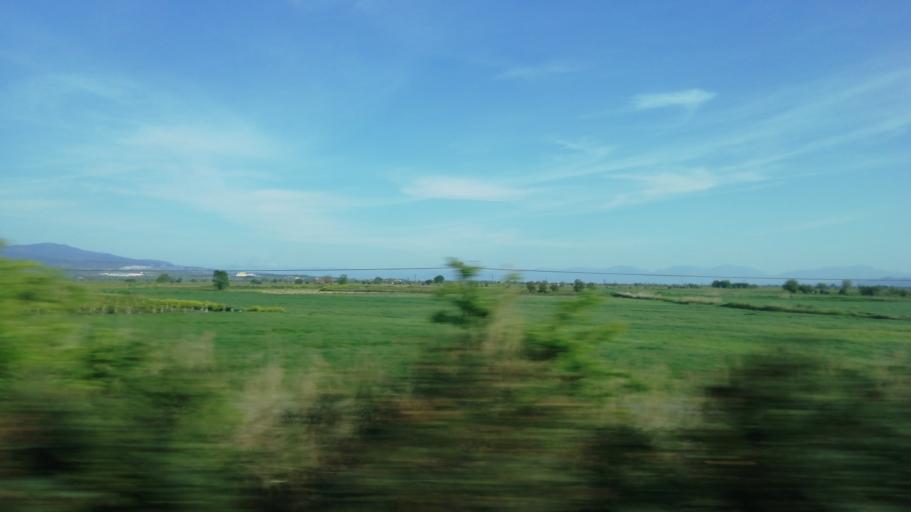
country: TR
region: Manisa
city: Saruhanli
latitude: 38.7151
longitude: 27.5507
